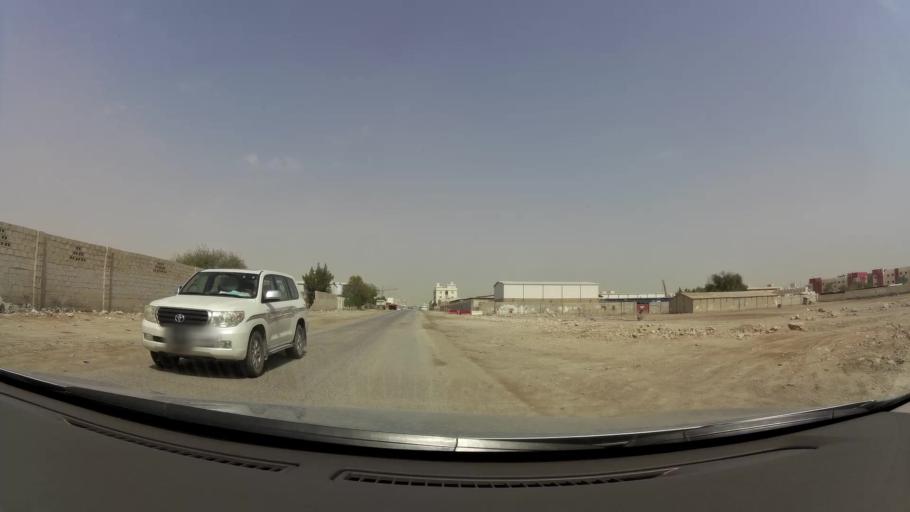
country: QA
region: Al Wakrah
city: Al Wukayr
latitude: 25.1653
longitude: 51.4424
